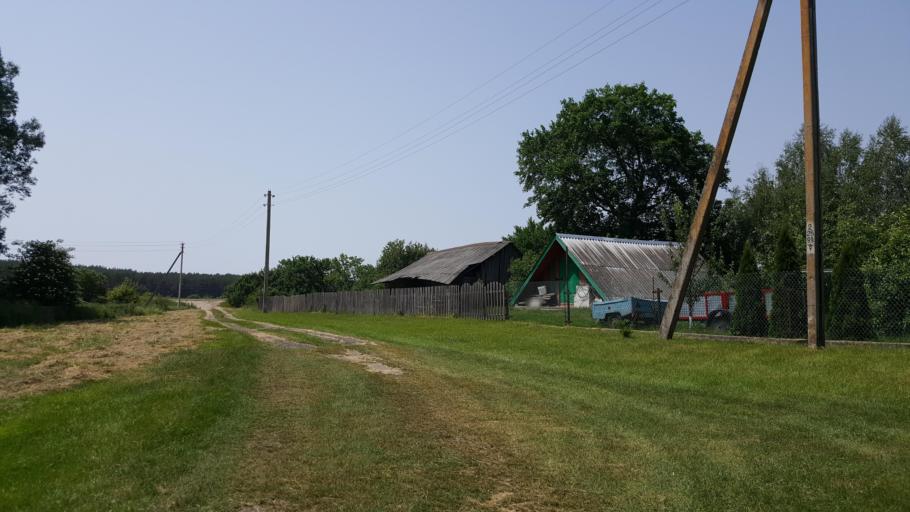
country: BY
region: Brest
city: Kamyanyuki
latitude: 52.4833
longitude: 23.8785
